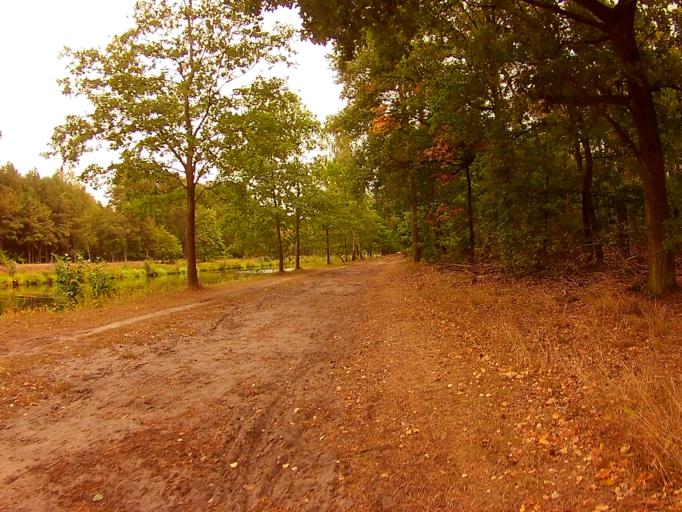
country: DE
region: Berlin
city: Schmockwitz
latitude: 52.3758
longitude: 13.6884
